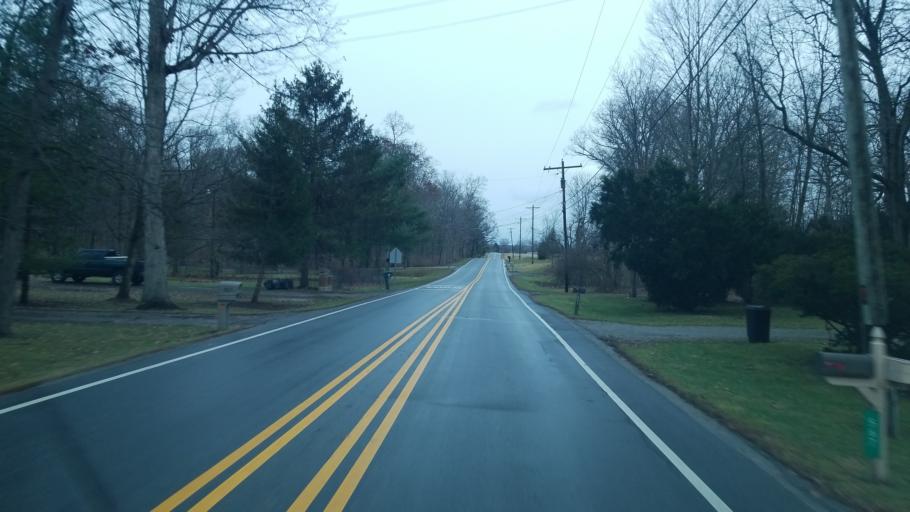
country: US
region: Ohio
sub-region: Delaware County
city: Delaware
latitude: 40.3503
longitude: -83.0856
